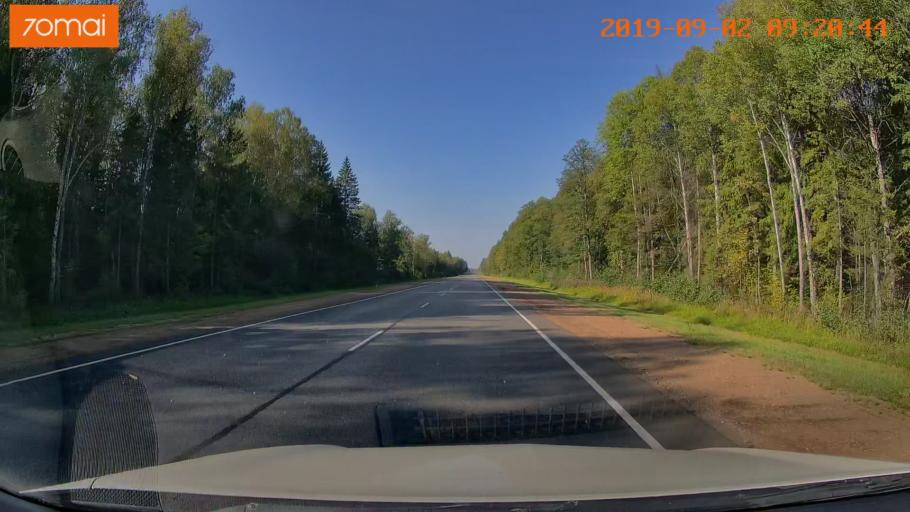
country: RU
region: Kaluga
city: Yukhnov
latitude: 54.7979
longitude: 35.3764
